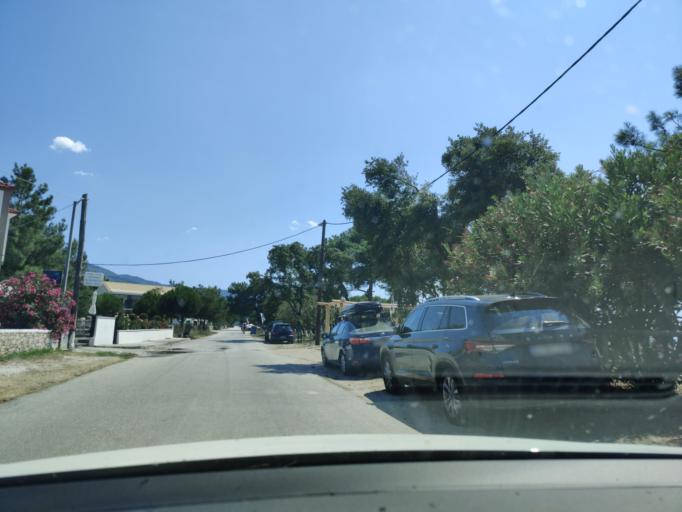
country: GR
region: East Macedonia and Thrace
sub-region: Nomos Kavalas
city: Prinos
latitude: 40.7597
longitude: 24.5617
